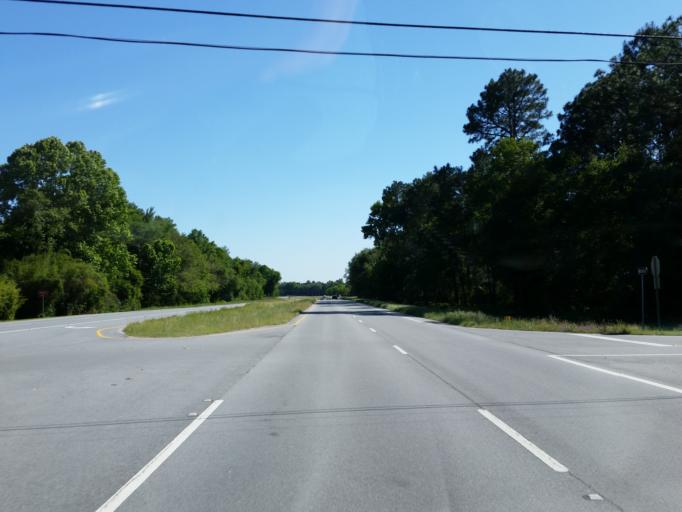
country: US
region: Georgia
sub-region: Lowndes County
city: Valdosta
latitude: 30.7478
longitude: -83.2186
